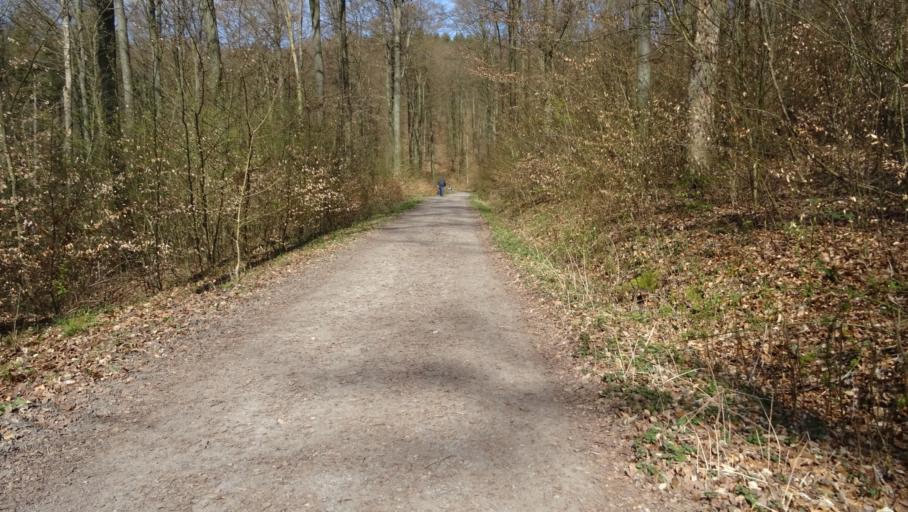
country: DE
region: Baden-Wuerttemberg
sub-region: Karlsruhe Region
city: Neckarzimmern
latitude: 49.3294
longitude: 9.1240
